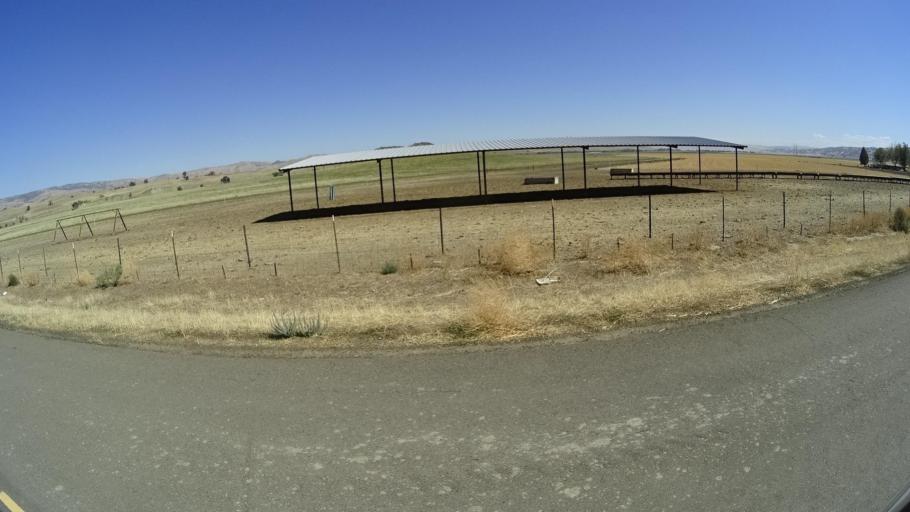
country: US
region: California
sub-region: San Luis Obispo County
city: Shandon
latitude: 35.8346
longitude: -120.3835
